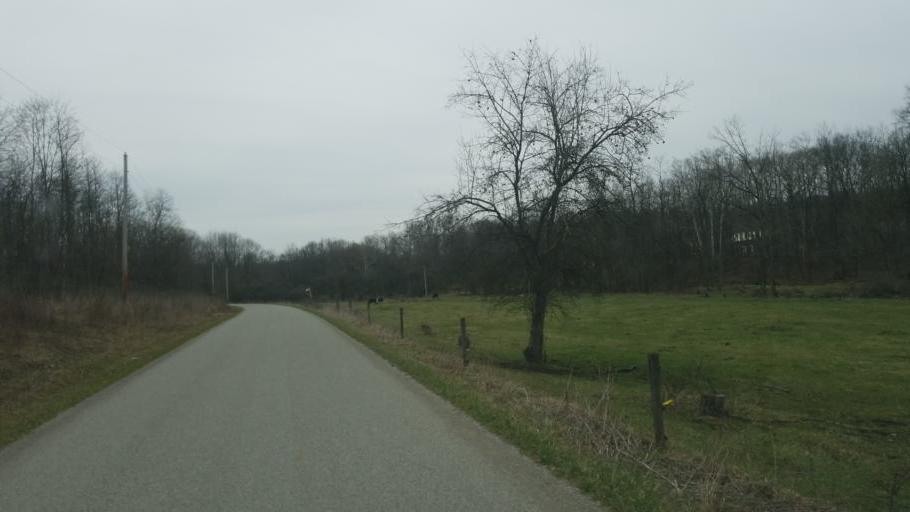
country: US
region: Ohio
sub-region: Knox County
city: Centerburg
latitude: 40.3588
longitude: -82.6491
